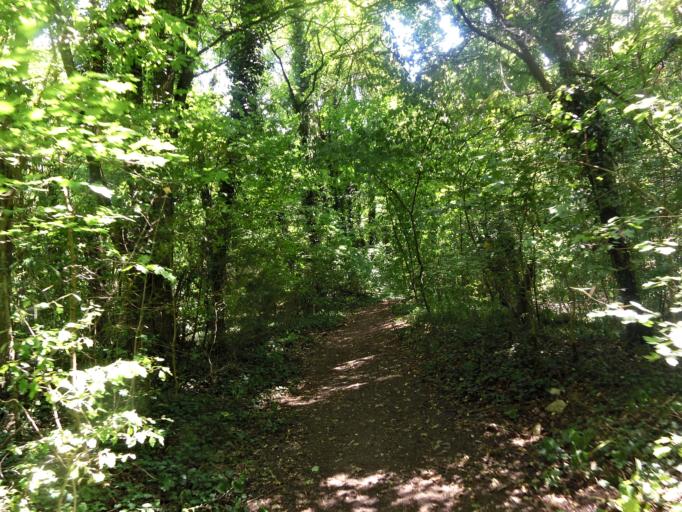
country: DE
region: Bavaria
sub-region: Regierungsbezirk Unterfranken
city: Randersacker
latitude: 49.7435
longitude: 9.9516
